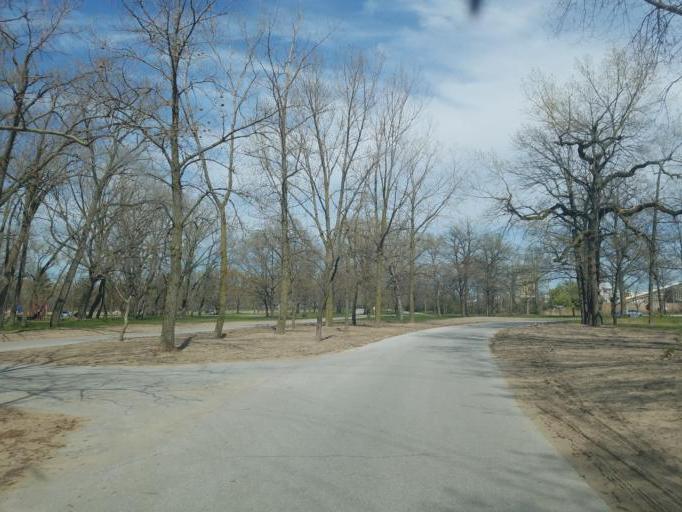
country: US
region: Ohio
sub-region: Lake County
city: Fairport Harbor
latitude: 41.7544
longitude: -81.2896
